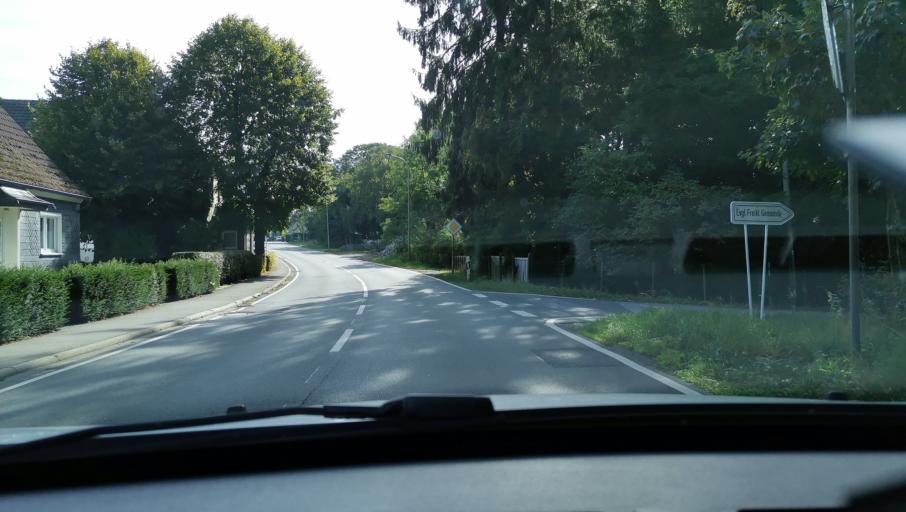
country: DE
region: North Rhine-Westphalia
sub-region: Regierungsbezirk Arnsberg
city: Breckerfeld
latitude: 51.2894
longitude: 7.4234
